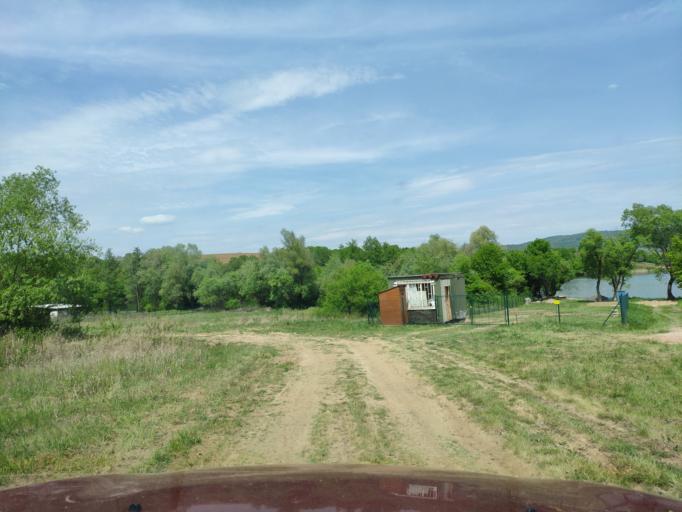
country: SK
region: Banskobystricky
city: Rimavska Sobota
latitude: 48.4758
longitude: 20.0837
